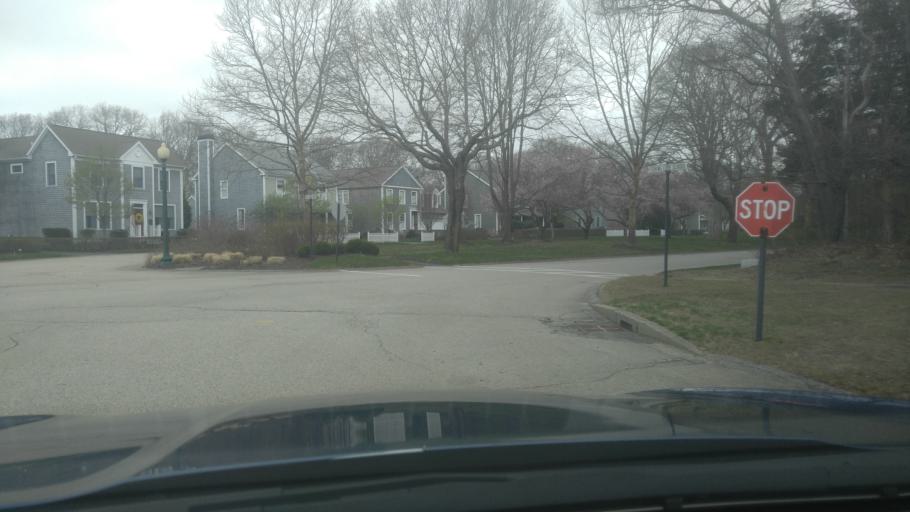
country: US
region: Rhode Island
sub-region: Washington County
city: North Kingstown
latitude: 41.5901
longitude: -71.4452
